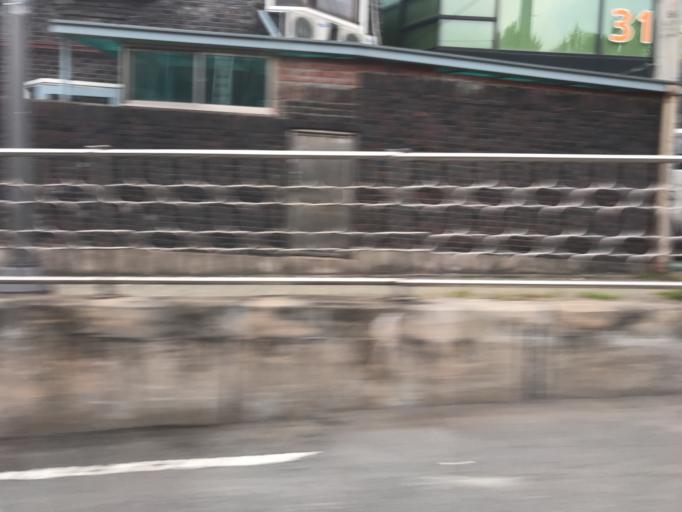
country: KR
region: Seoul
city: Seoul
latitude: 37.5672
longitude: 126.9471
